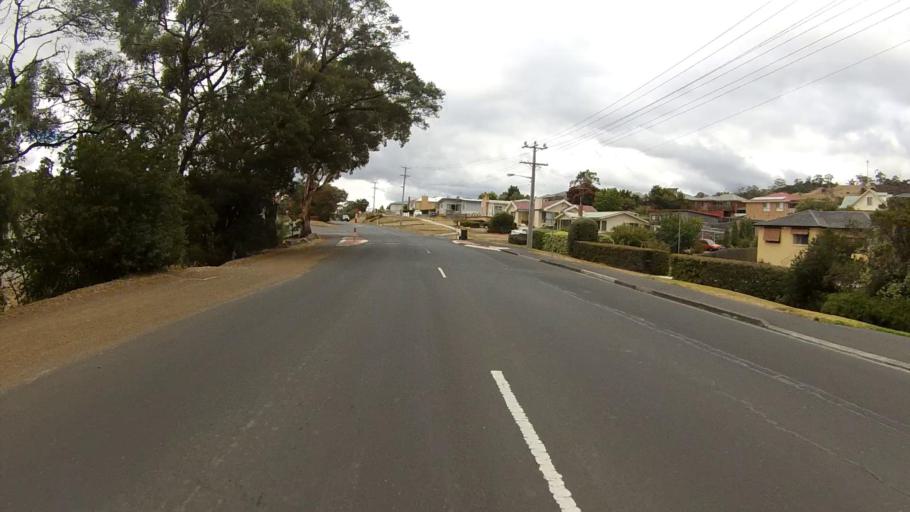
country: AU
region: Tasmania
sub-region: Glenorchy
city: Austins Ferry
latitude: -42.7725
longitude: 147.2481
